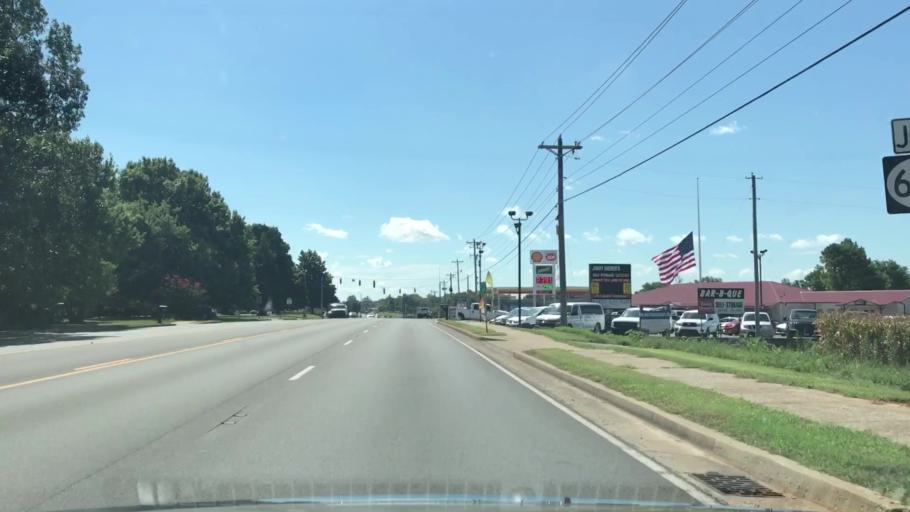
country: US
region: Kentucky
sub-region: Warren County
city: Plano
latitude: 36.9216
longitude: -86.4096
